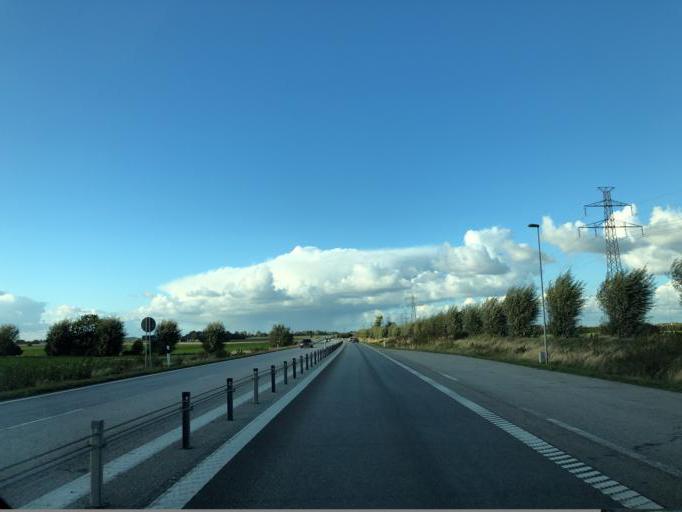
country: SE
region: Skane
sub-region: Lunds Kommun
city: Lund
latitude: 55.7252
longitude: 13.1496
